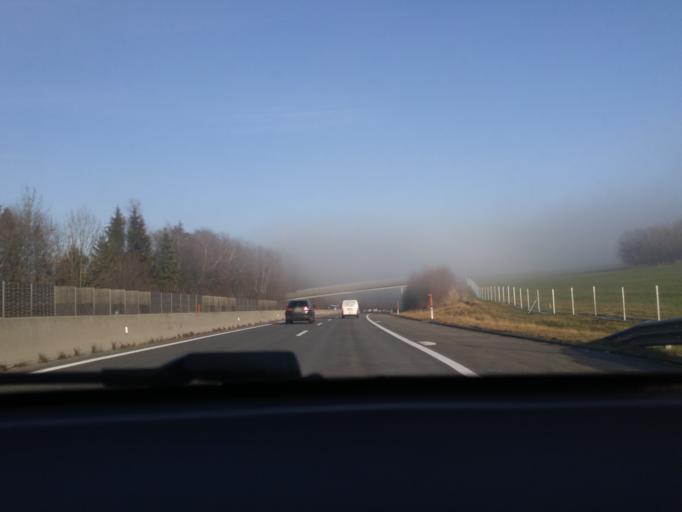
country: AT
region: Upper Austria
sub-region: Politischer Bezirk Vocklabruck
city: Attersee
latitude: 47.9497
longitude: 13.5236
